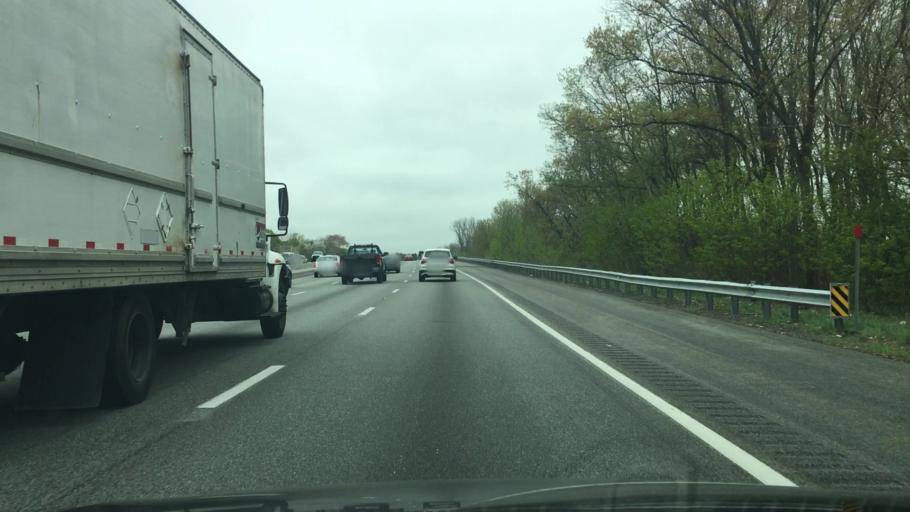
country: US
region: Massachusetts
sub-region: Essex County
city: Lynnfield
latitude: 42.5214
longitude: -71.0560
